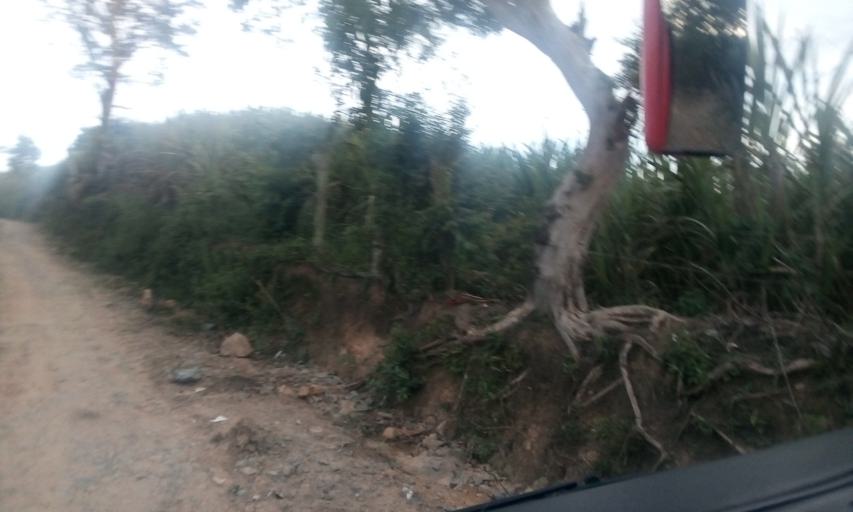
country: CO
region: Boyaca
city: Santana
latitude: 6.0051
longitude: -73.5072
